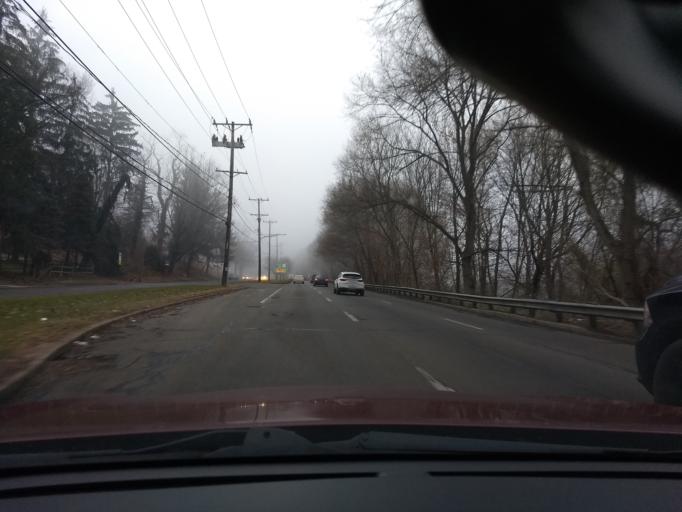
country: US
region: Pennsylvania
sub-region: Allegheny County
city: Braddock Hills
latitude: 40.4290
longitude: -79.8635
